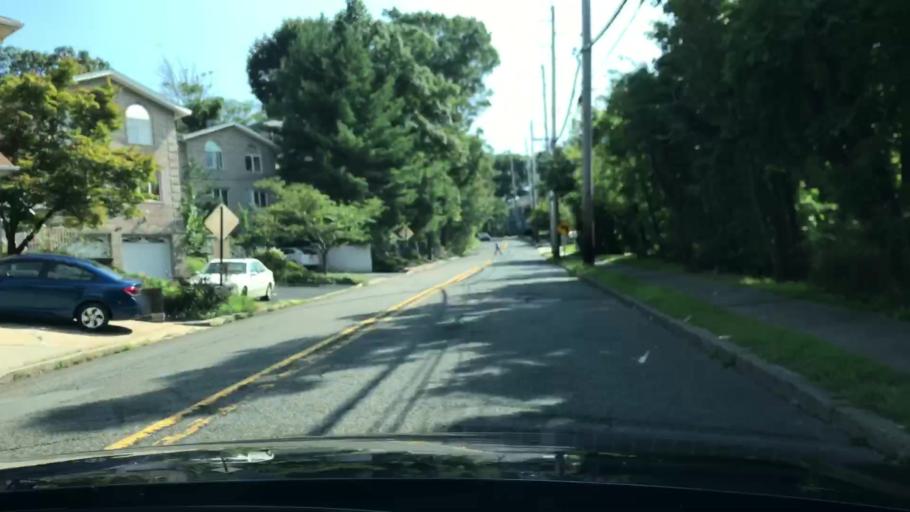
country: US
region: New Jersey
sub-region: Bergen County
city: Ridgefield
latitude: 40.8284
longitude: -73.9985
